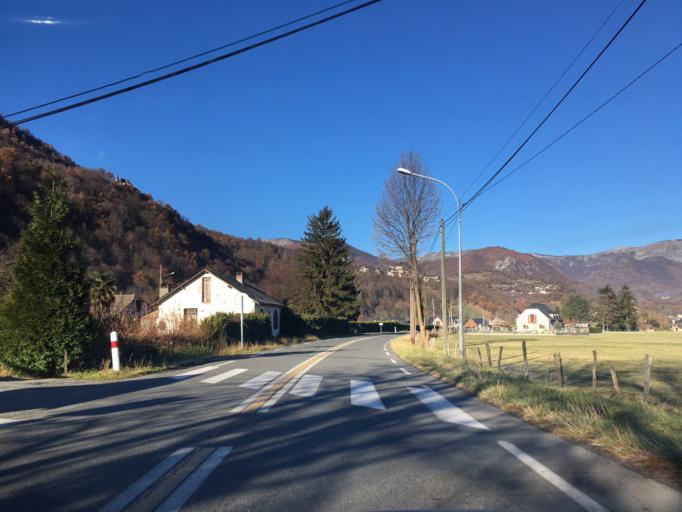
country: FR
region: Midi-Pyrenees
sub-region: Departement des Hautes-Pyrenees
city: Pierrefitte-Nestalas
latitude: 42.9749
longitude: -0.0782
